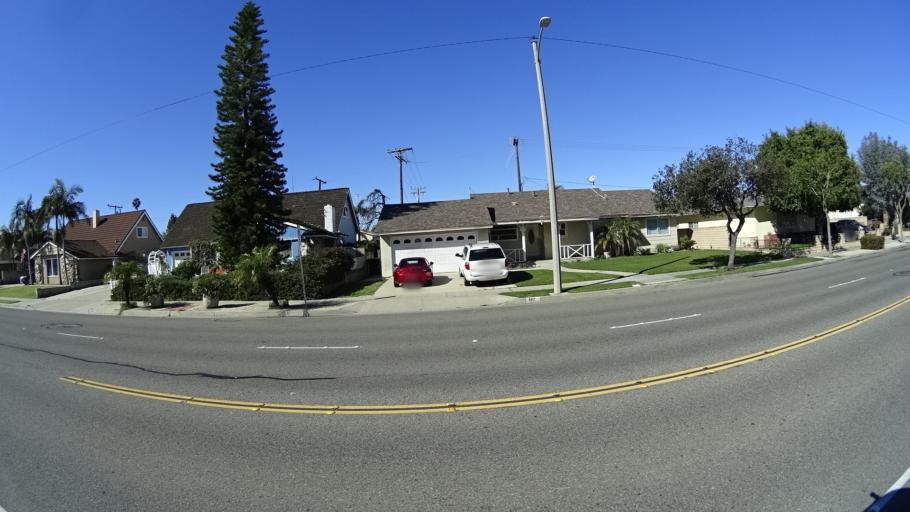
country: US
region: California
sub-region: Orange County
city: Placentia
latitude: 33.8418
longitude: -117.8803
